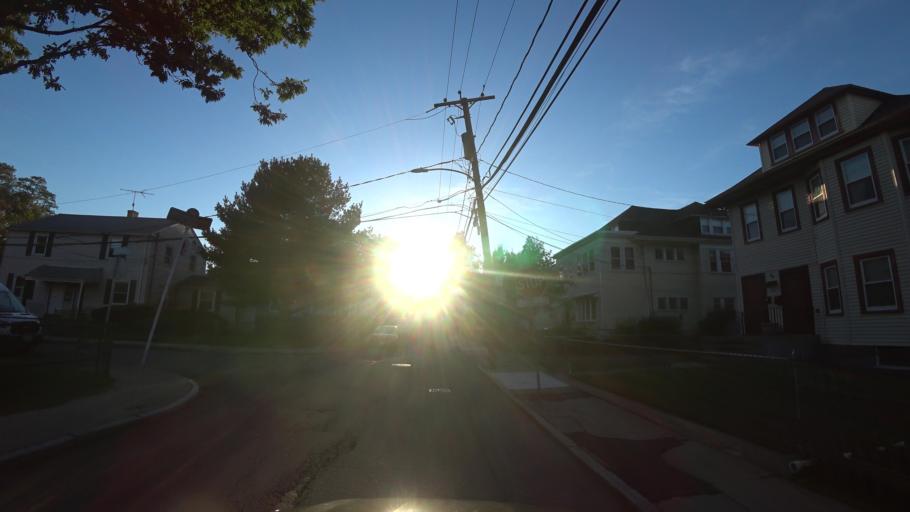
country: US
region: Massachusetts
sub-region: Norfolk County
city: Milton
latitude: 42.2737
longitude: -71.0739
